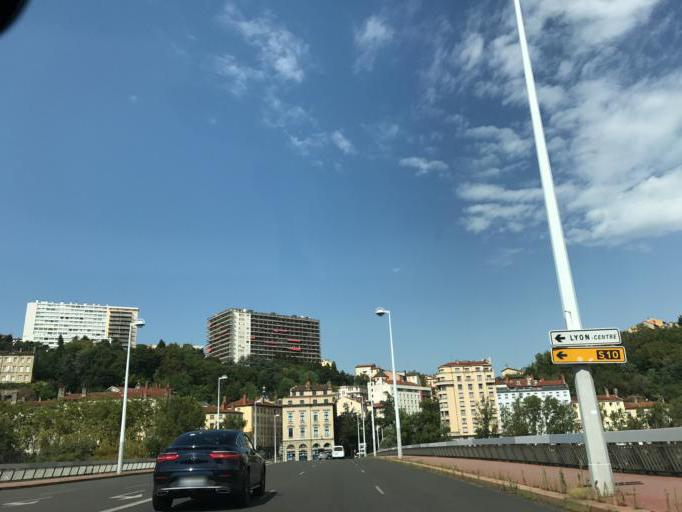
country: FR
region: Rhone-Alpes
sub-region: Departement du Rhone
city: Caluire-et-Cuire
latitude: 45.7784
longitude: 4.8435
